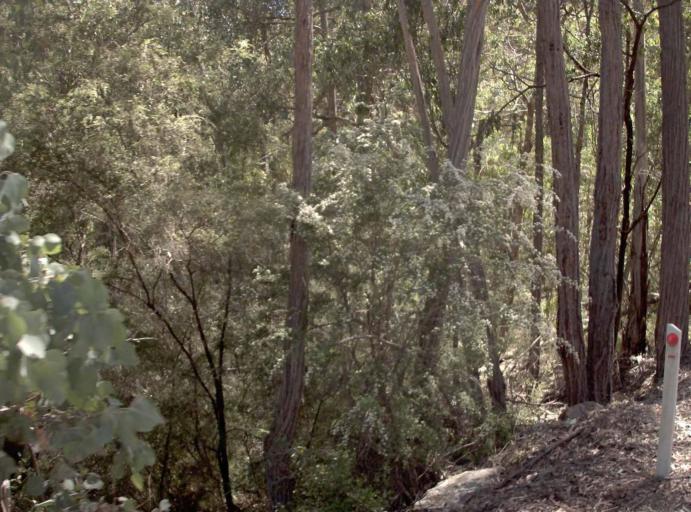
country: AU
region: Victoria
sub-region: East Gippsland
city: Lakes Entrance
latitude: -37.3859
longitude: 148.2179
